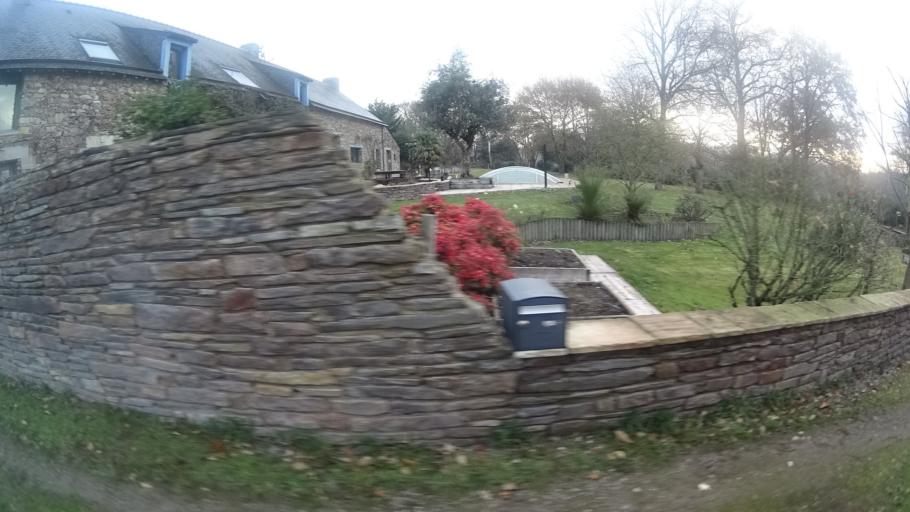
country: FR
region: Pays de la Loire
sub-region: Departement de la Loire-Atlantique
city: Saint-Nicolas-de-Redon
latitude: 47.6369
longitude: -2.0411
